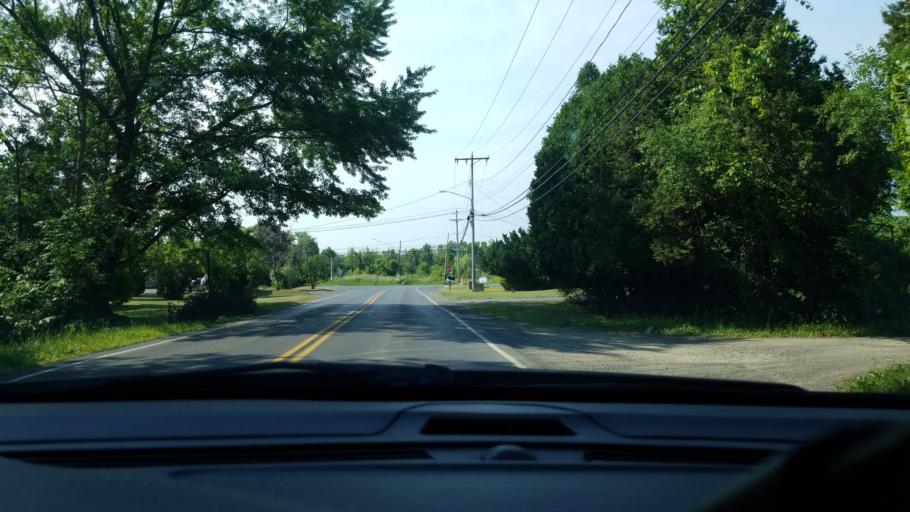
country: US
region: New York
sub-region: Onondaga County
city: East Syracuse
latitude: 43.1028
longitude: -76.0725
